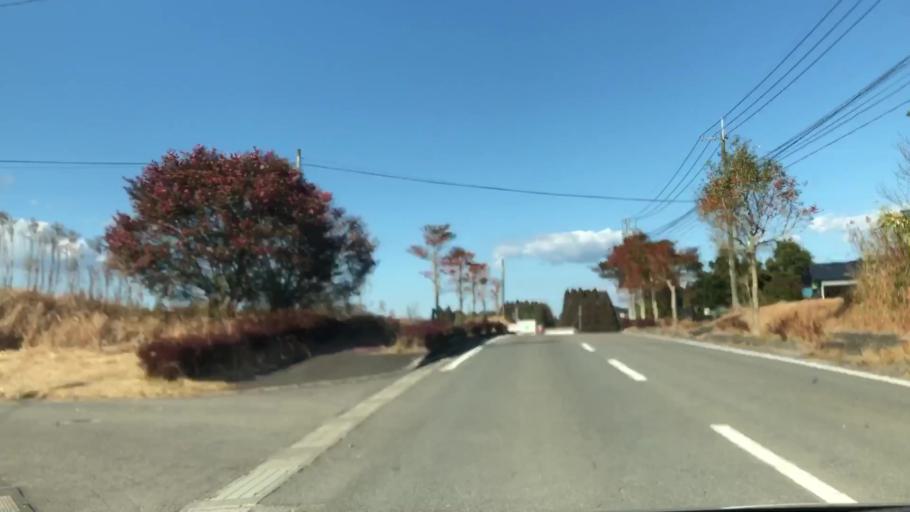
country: JP
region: Kagoshima
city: Satsumasendai
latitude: 31.8374
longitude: 130.4300
